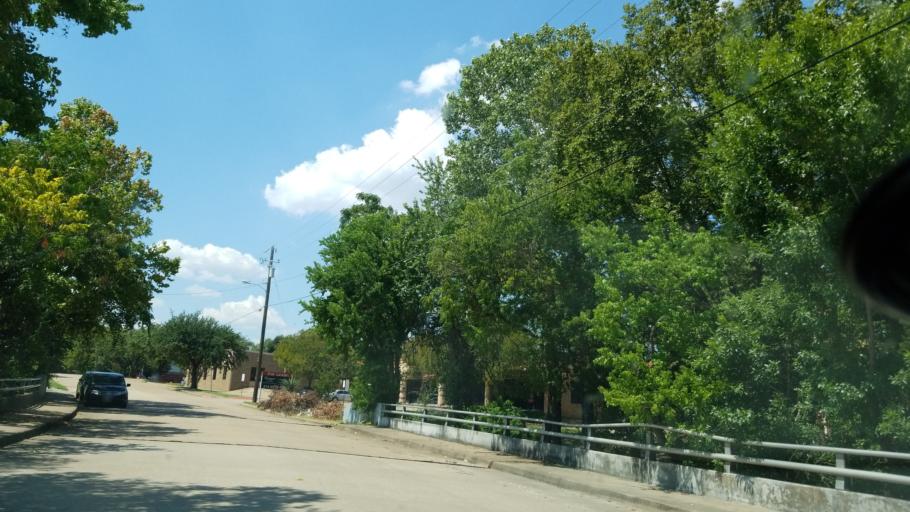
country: US
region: Texas
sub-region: Dallas County
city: Garland
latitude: 32.8819
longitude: -96.6987
